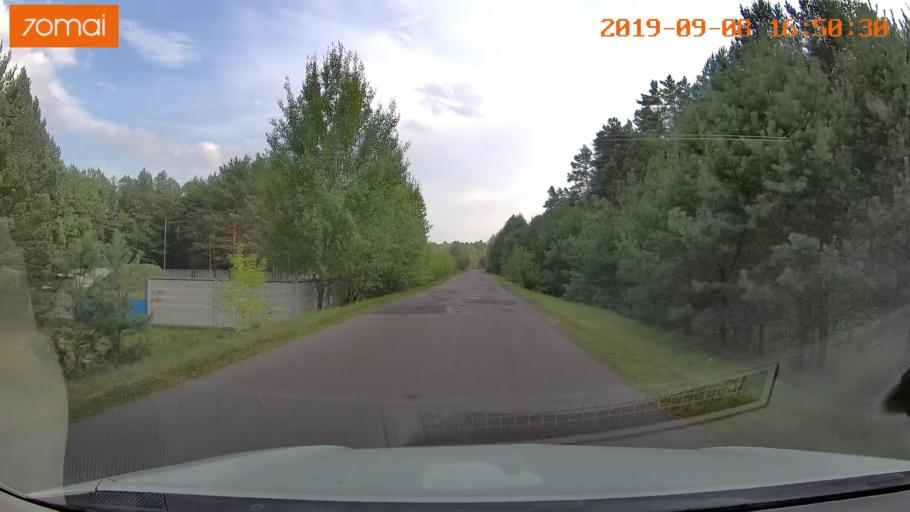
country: BY
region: Grodnenskaya
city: Hrodna
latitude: 53.7989
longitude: 23.8887
